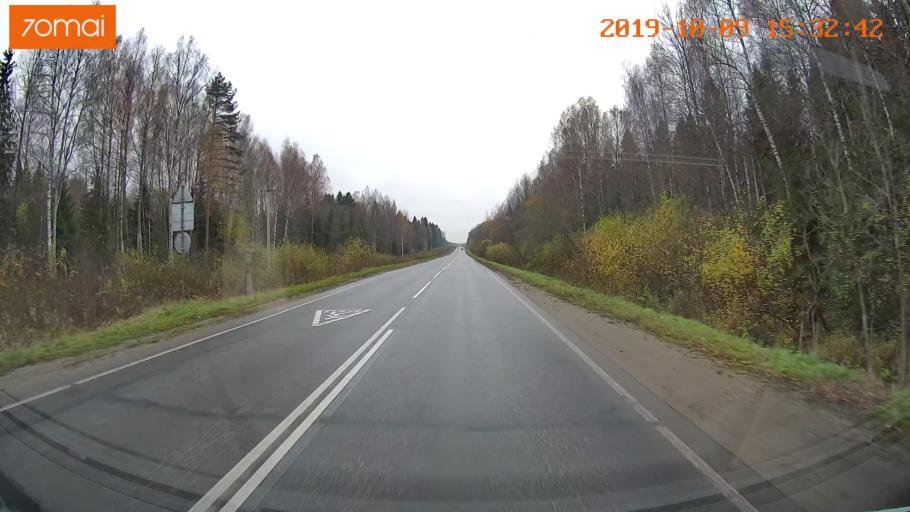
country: RU
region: Kostroma
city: Oktyabr'skiy
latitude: 57.9618
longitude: 41.2724
